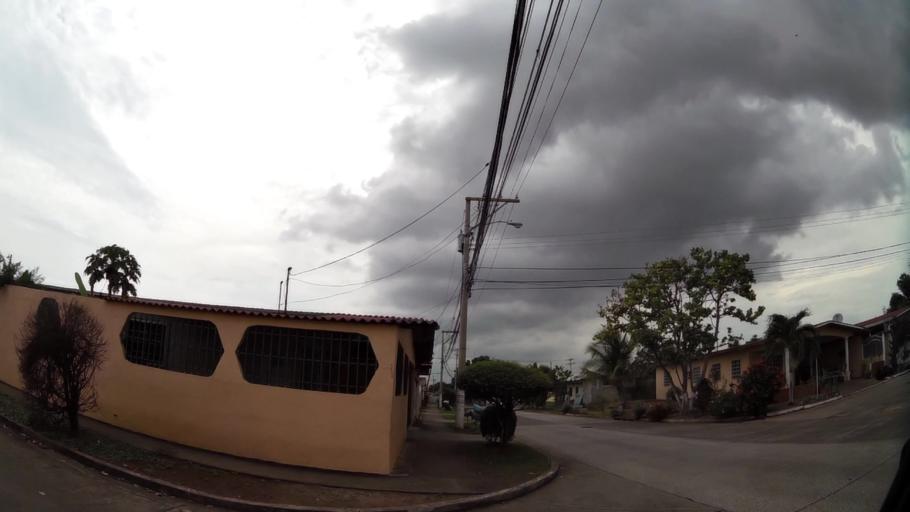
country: PA
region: Panama
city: Tocumen
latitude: 9.0481
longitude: -79.4090
